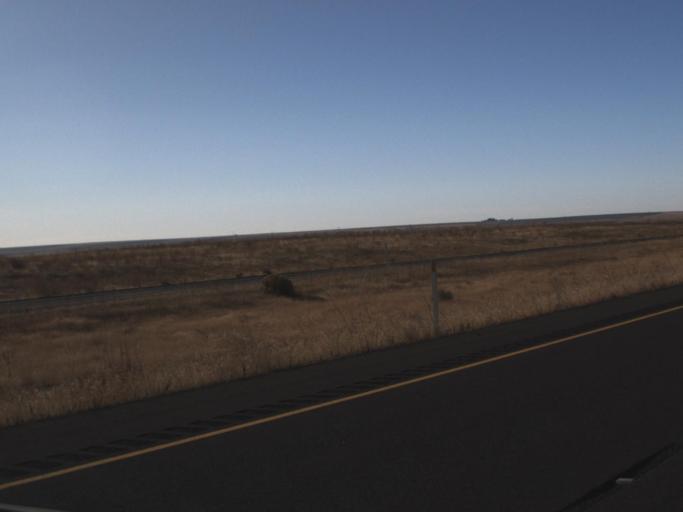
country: US
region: Washington
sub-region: Franklin County
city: Connell
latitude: 46.6791
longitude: -118.8434
